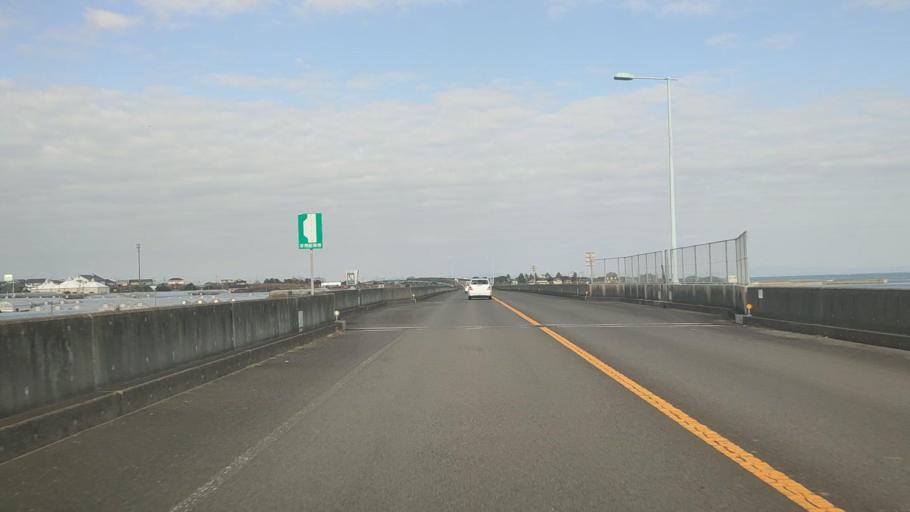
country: JP
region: Nagasaki
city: Shimabara
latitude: 32.7324
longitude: 130.3677
